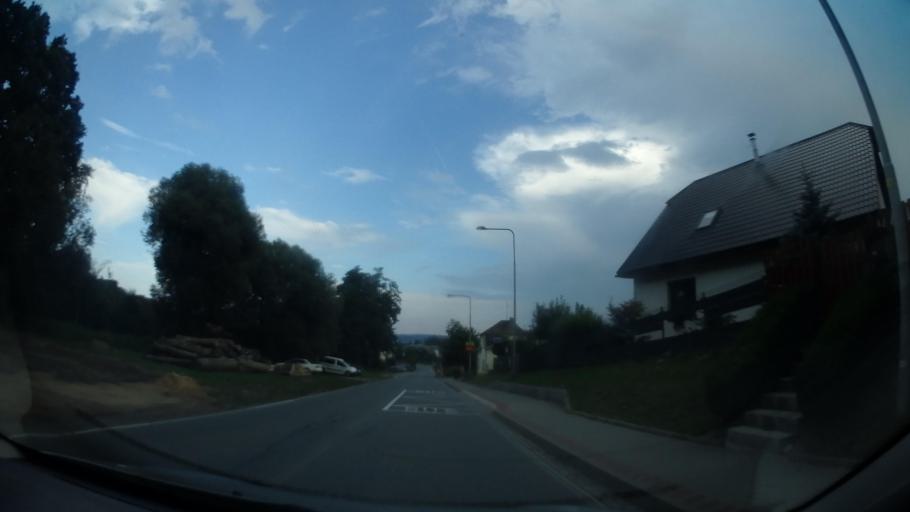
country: CZ
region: Olomoucky
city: Zabreh
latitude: 49.8867
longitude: 16.8507
